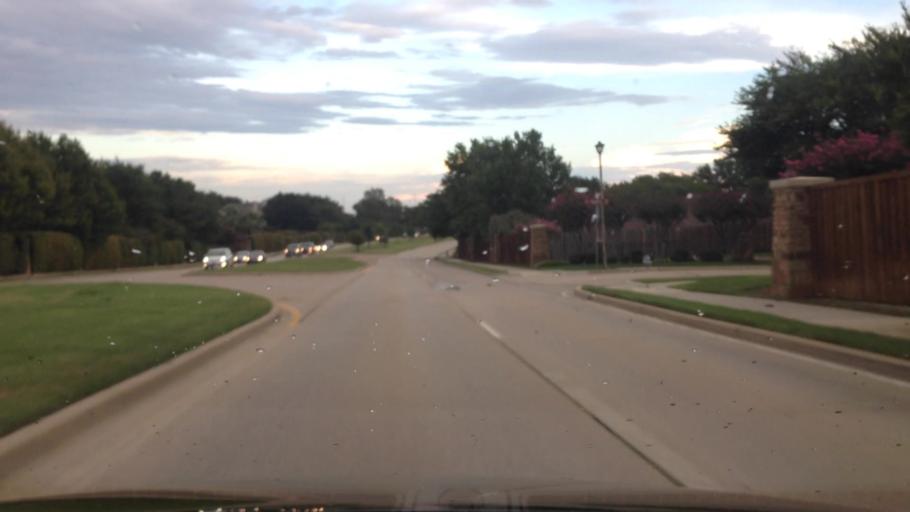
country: US
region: Texas
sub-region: Denton County
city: Flower Mound
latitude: 33.0167
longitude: -97.0499
